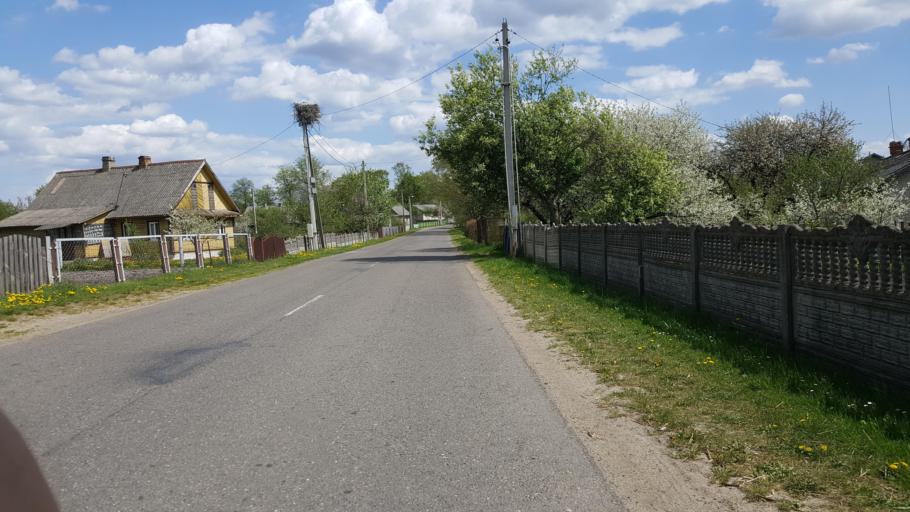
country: BY
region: Brest
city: Zhabinka
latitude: 52.4257
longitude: 24.1557
